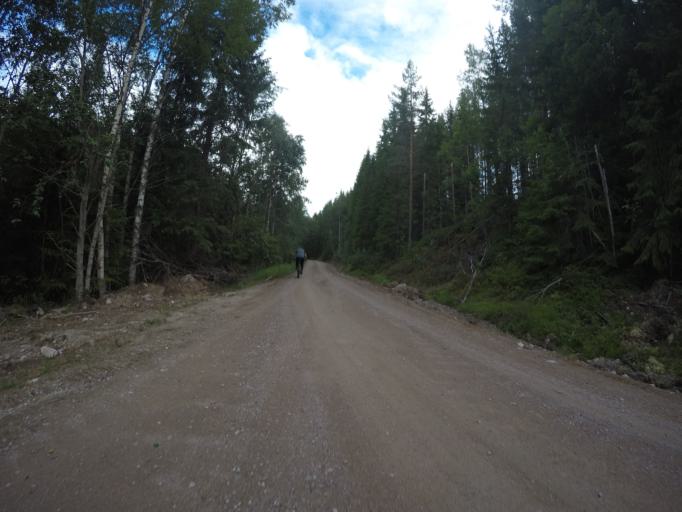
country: SE
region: Vaermland
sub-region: Filipstads Kommun
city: Lesjofors
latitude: 60.0105
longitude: 14.4077
